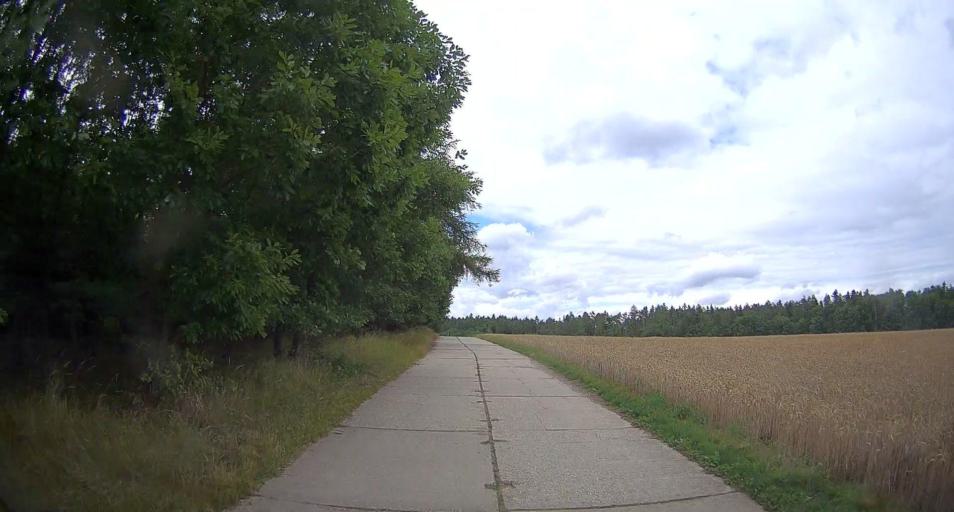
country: CZ
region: South Moravian
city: Lipuvka
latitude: 49.3332
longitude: 16.5362
